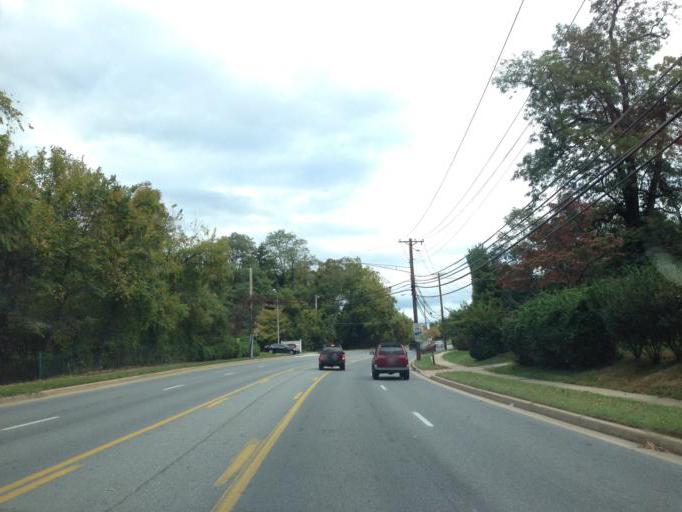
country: US
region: Maryland
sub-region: Baltimore County
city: Pikesville
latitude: 39.3771
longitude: -76.7347
